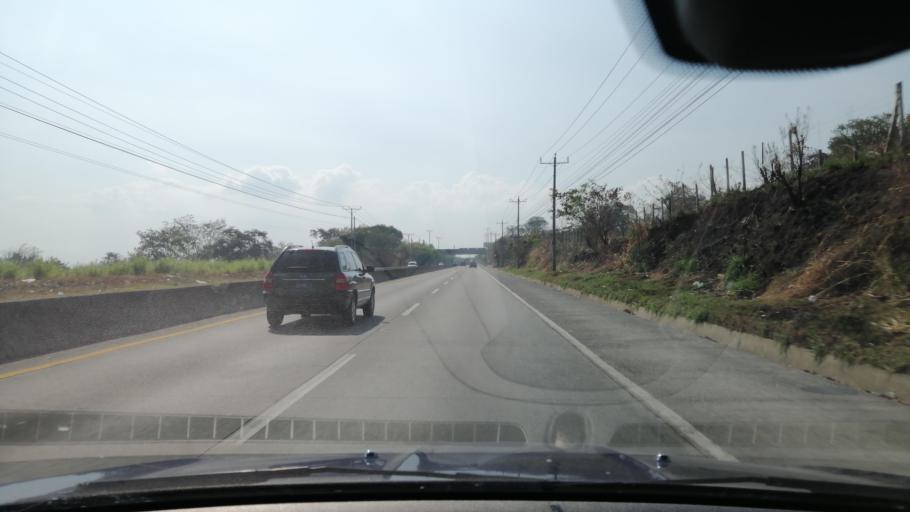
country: SV
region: San Salvador
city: Apopa
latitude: 13.7890
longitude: -89.2201
